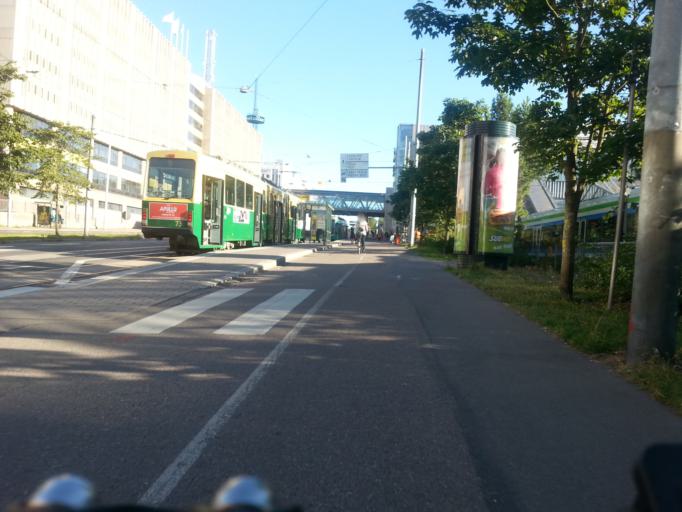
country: FI
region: Uusimaa
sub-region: Helsinki
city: Helsinki
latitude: 60.1997
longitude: 24.9341
